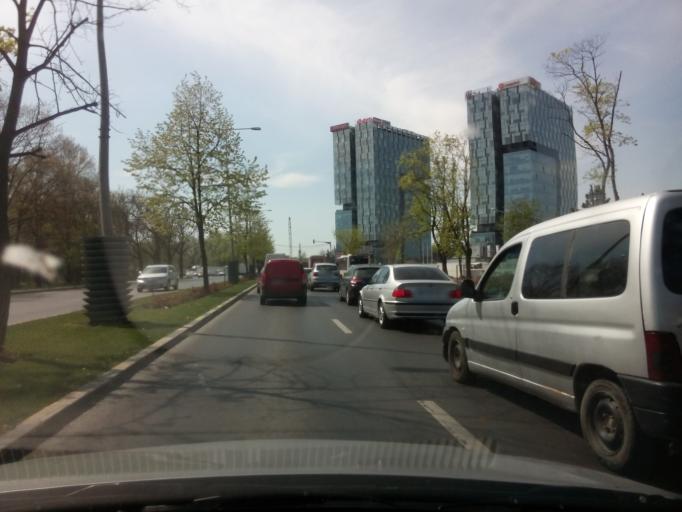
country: RO
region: Bucuresti
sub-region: Municipiul Bucuresti
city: Bucuresti
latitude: 44.4797
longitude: 26.0736
